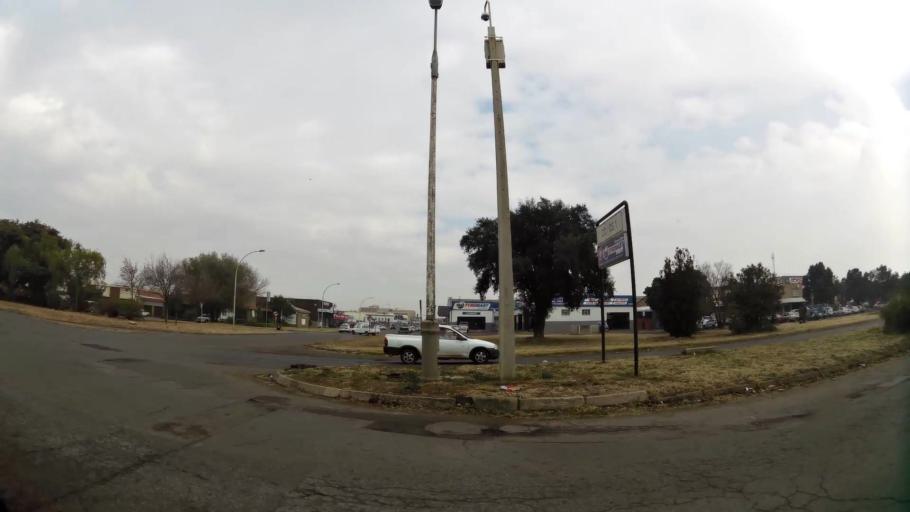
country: ZA
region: Gauteng
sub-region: Sedibeng District Municipality
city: Vanderbijlpark
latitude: -26.7000
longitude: 27.8406
